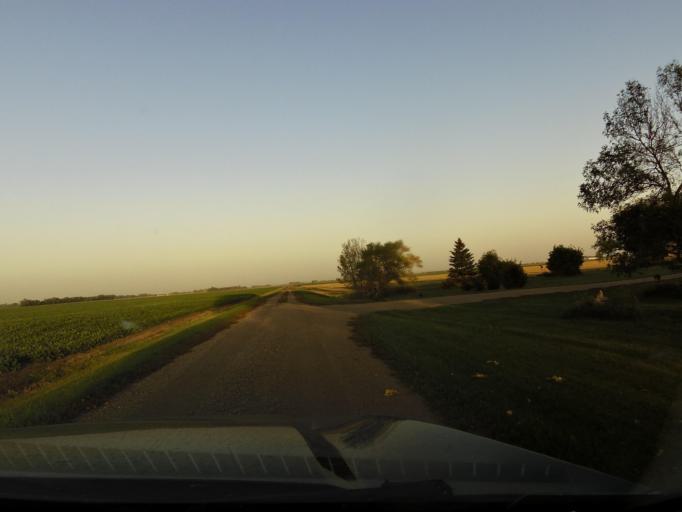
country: US
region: North Dakota
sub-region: Walsh County
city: Grafton
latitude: 48.3831
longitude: -97.2534
